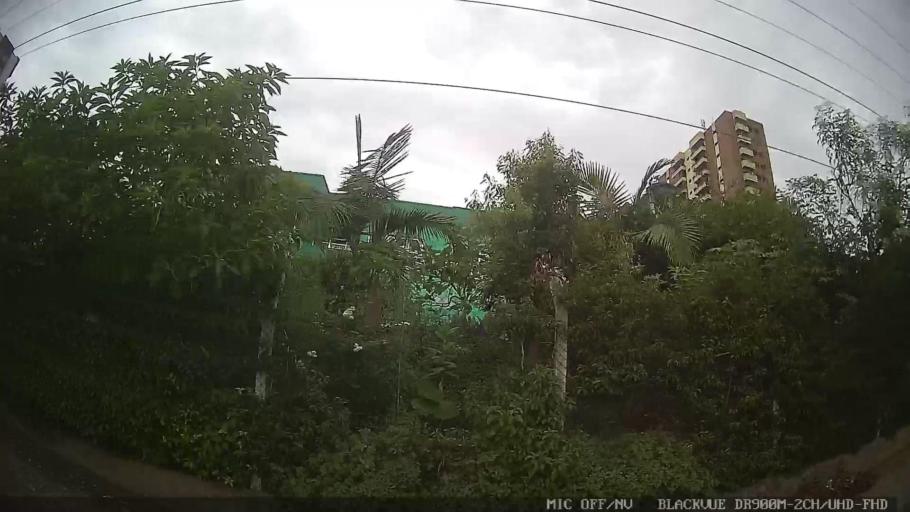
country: BR
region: Sao Paulo
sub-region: Maua
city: Maua
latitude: -23.6743
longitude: -46.4614
